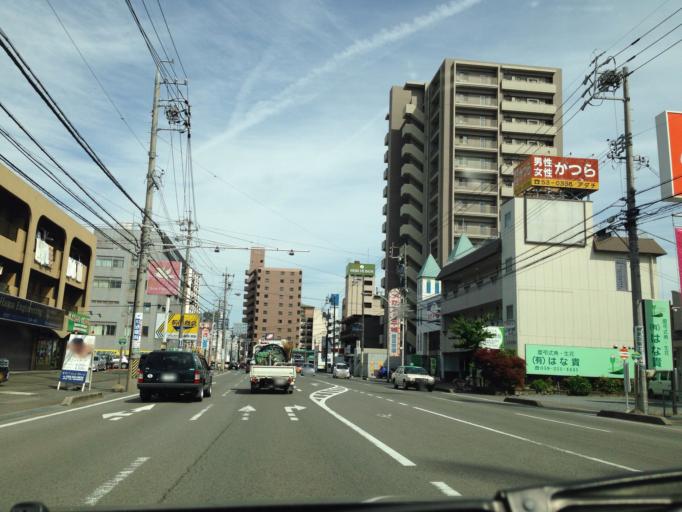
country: JP
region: Mie
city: Yokkaichi
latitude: 34.9735
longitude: 136.6108
